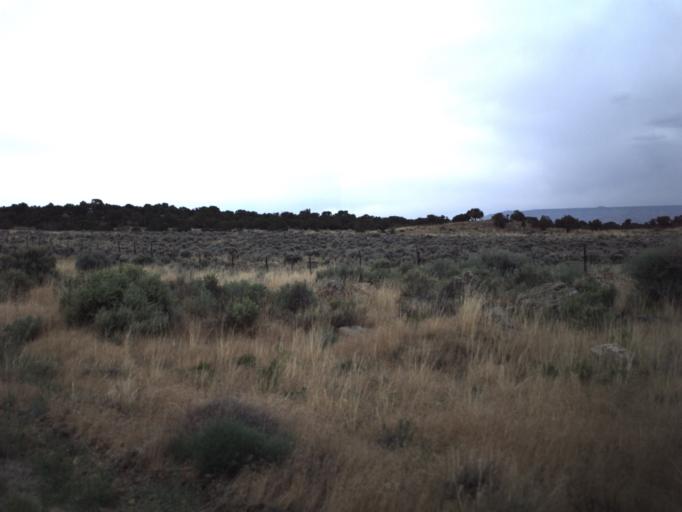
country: US
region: Utah
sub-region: Carbon County
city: East Carbon City
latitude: 39.4775
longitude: -110.3991
